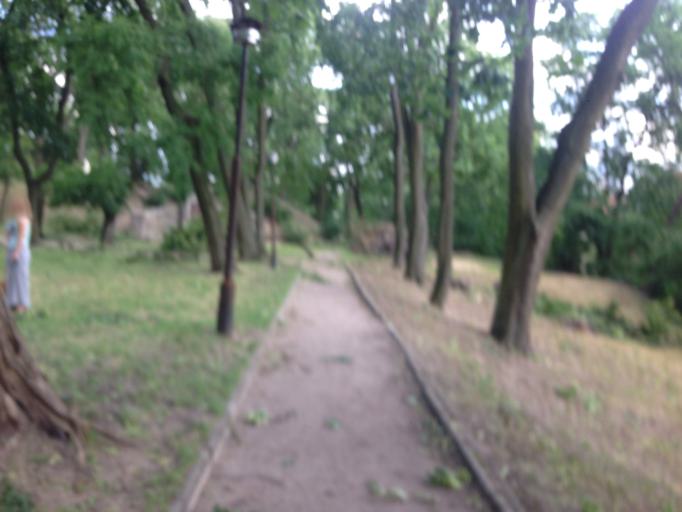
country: PL
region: Warmian-Masurian Voivodeship
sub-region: Powiat nidzicki
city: Nidzica
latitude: 53.3592
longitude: 20.4289
